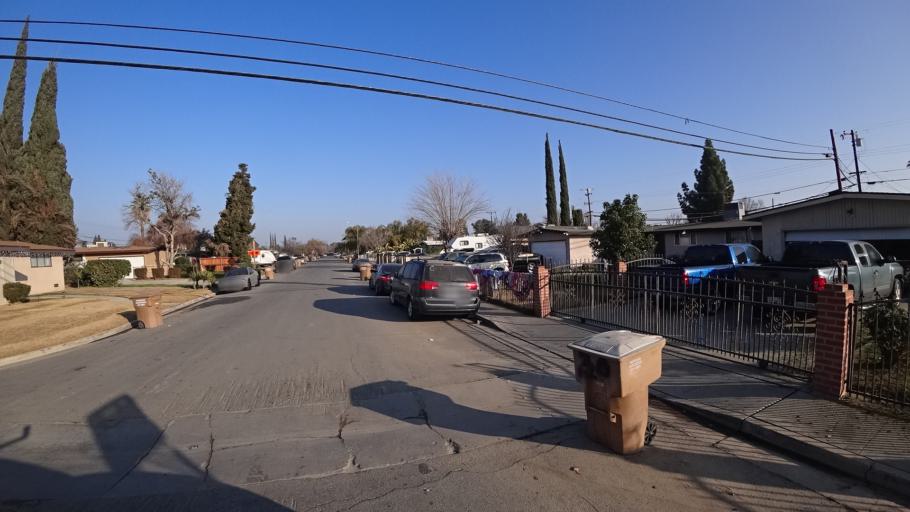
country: US
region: California
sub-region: Kern County
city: Bakersfield
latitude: 35.3557
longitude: -119.0481
